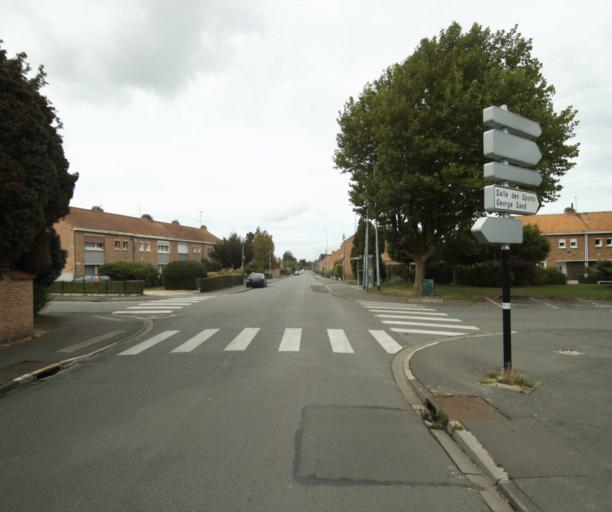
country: FR
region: Nord-Pas-de-Calais
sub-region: Departement du Nord
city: Faches-Thumesnil
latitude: 50.5946
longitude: 3.0760
